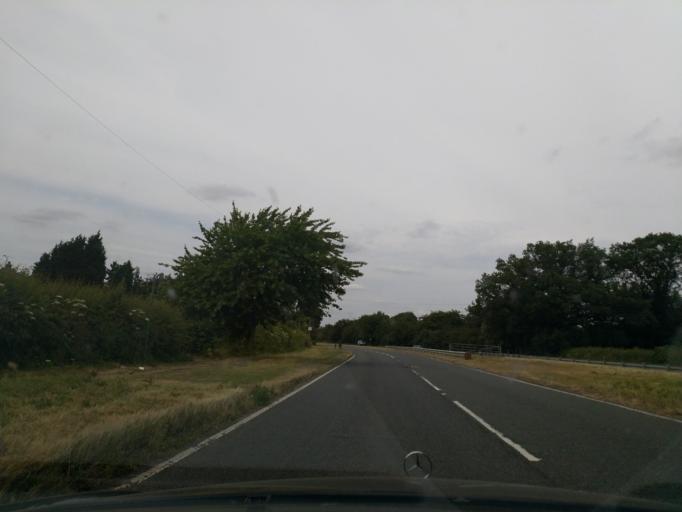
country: GB
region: England
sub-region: Solihull
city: Balsall Common
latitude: 52.4092
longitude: -1.6652
